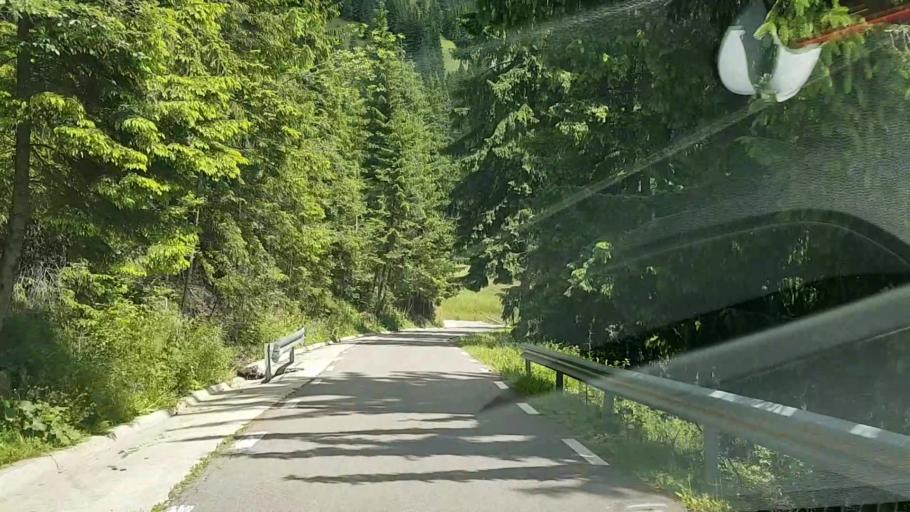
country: RO
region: Suceava
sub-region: Municipiul Campulung Moldovenesc
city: Campulung Moldovenesc
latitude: 47.4378
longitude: 25.5562
